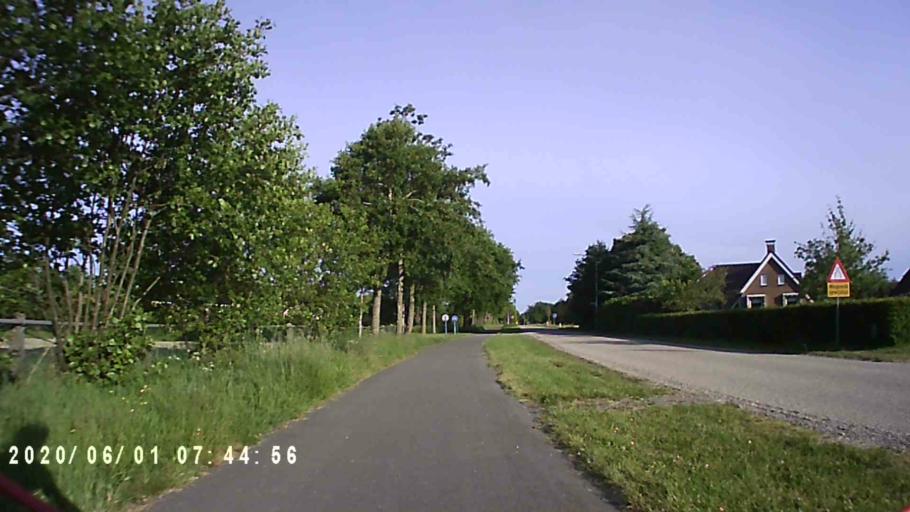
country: NL
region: Friesland
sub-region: Gemeente Dantumadiel
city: Rinsumageast
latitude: 53.2922
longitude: 5.9650
